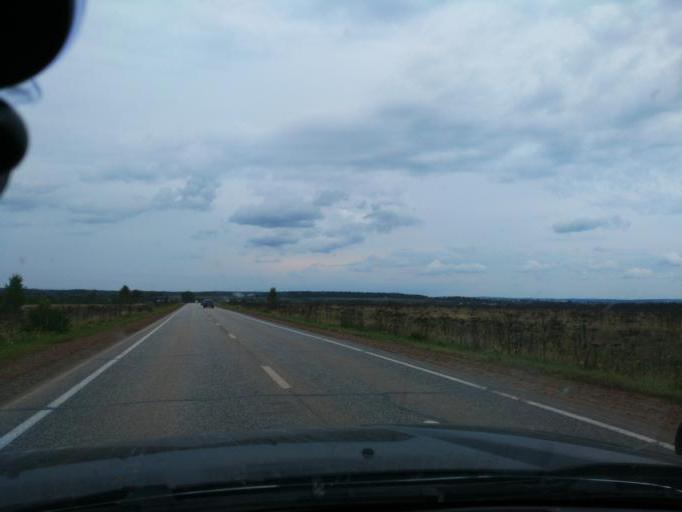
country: RU
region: Perm
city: Chernushka
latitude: 56.5072
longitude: 55.9978
